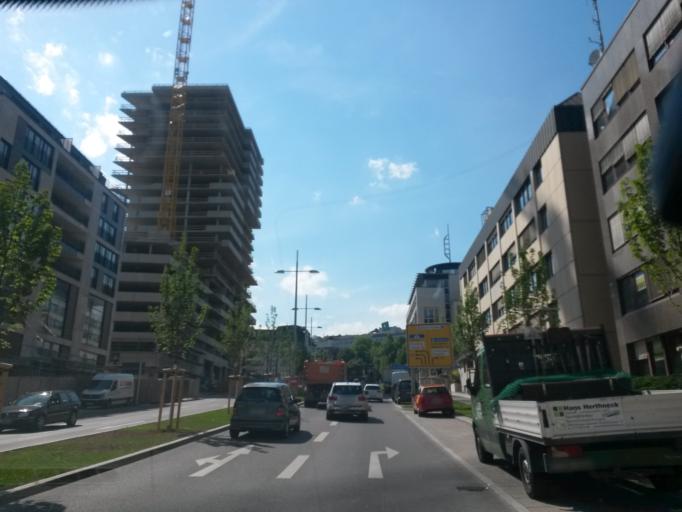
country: DE
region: Baden-Wuerttemberg
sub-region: Regierungsbezirk Stuttgart
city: Stuttgart
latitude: 48.7921
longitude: 9.1839
